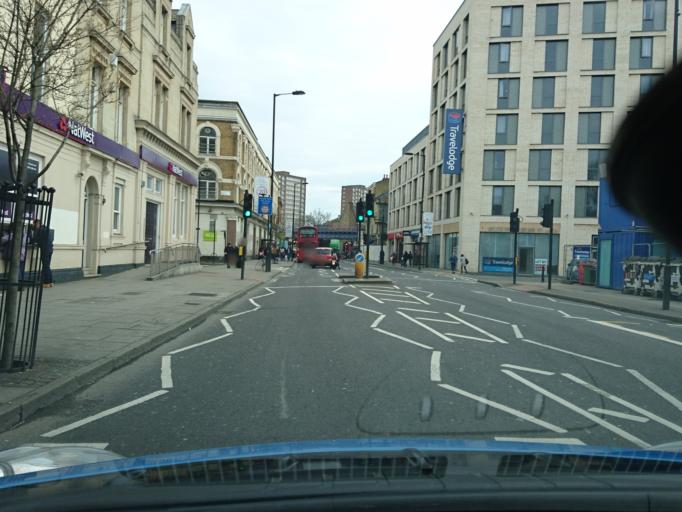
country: GB
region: England
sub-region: Greater London
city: Hackney
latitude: 51.5479
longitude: -0.0566
